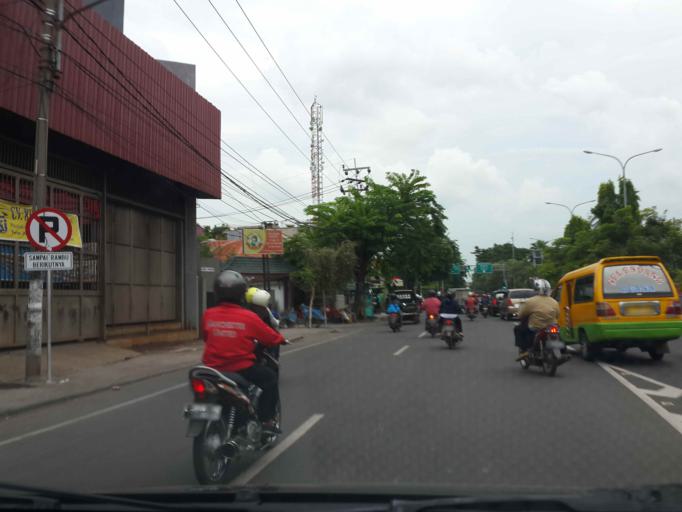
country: ID
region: East Java
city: Gubengairlangga
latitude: -7.2773
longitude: 112.7286
